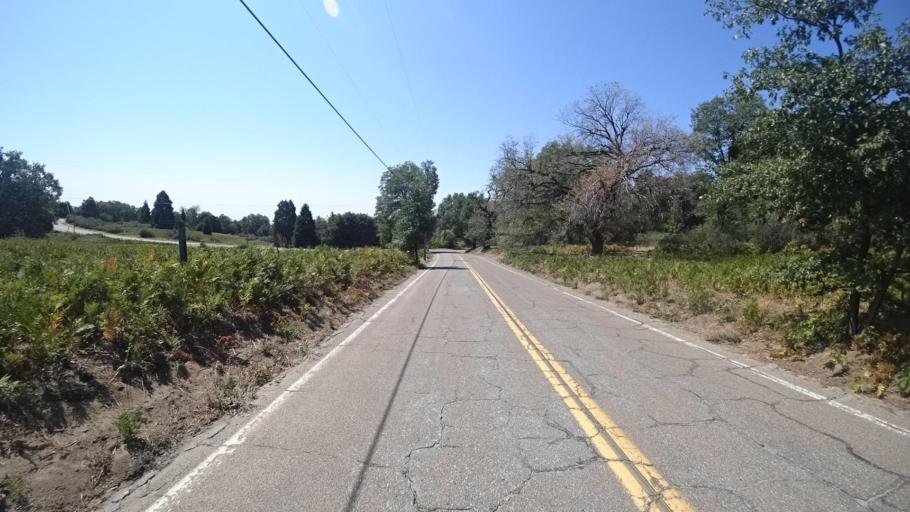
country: US
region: California
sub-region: Riverside County
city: Aguanga
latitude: 33.3194
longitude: -116.8802
